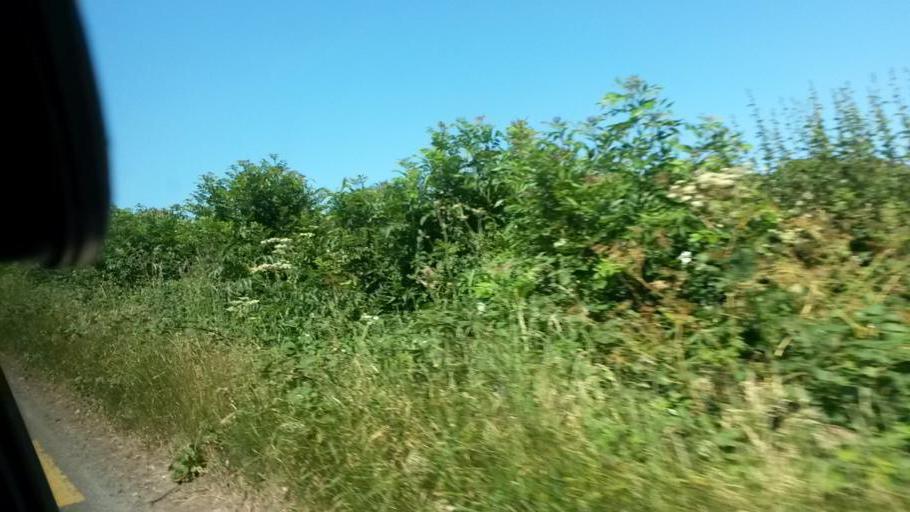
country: IE
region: Leinster
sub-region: An Mhi
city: Stamullin
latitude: 53.5571
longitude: -6.2724
